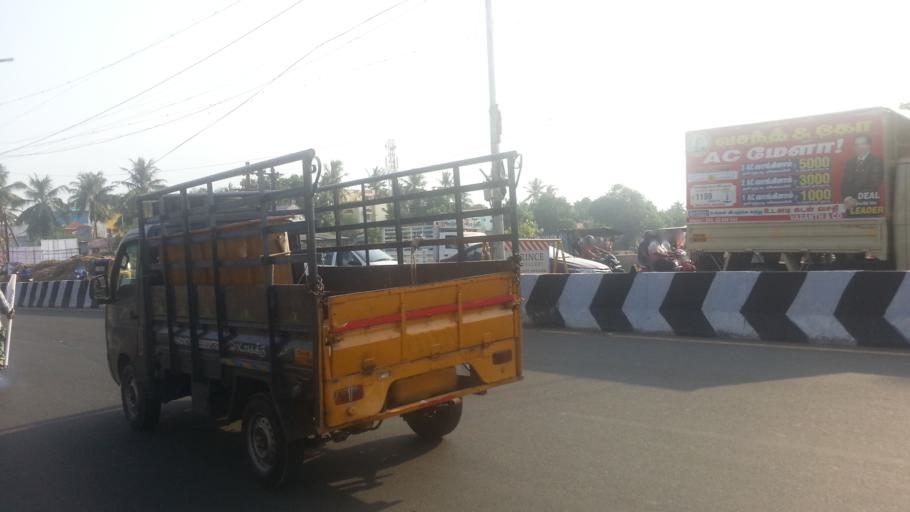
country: IN
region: Tamil Nadu
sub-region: Kancheepuram
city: Alandur
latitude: 12.9873
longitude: 80.2185
